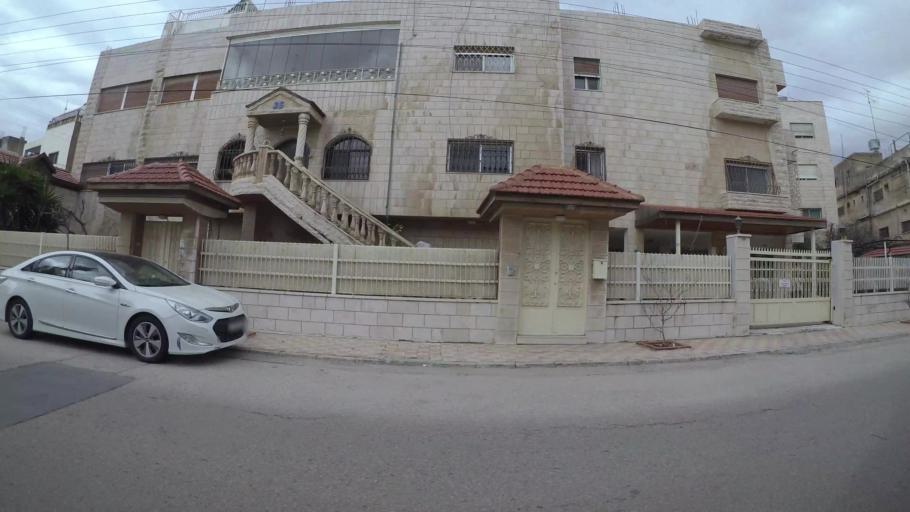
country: JO
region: Amman
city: Wadi as Sir
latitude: 31.9500
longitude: 35.8354
